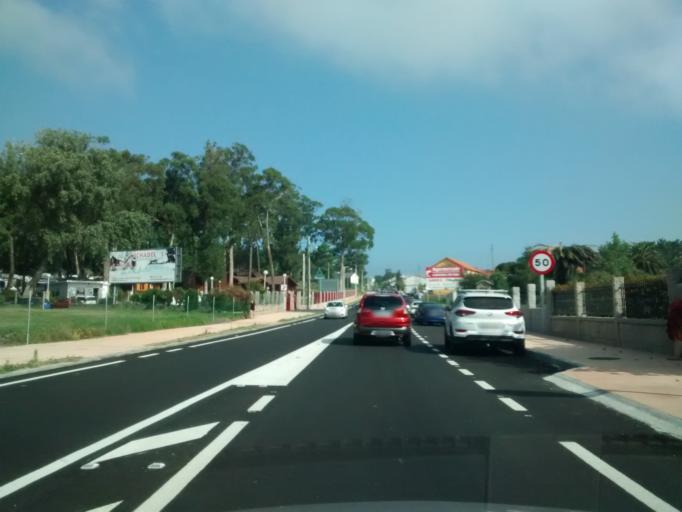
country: ES
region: Galicia
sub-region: Provincia de Pontevedra
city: Sanxenxo
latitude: 42.4171
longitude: -8.8686
